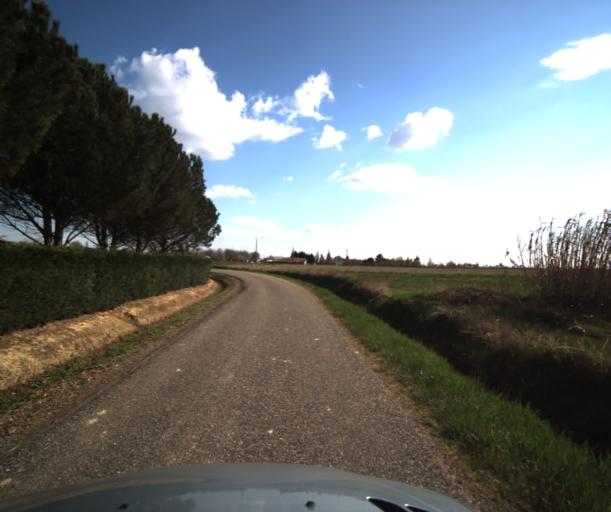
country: FR
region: Midi-Pyrenees
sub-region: Departement du Tarn-et-Garonne
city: Bressols
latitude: 43.9697
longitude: 1.2942
